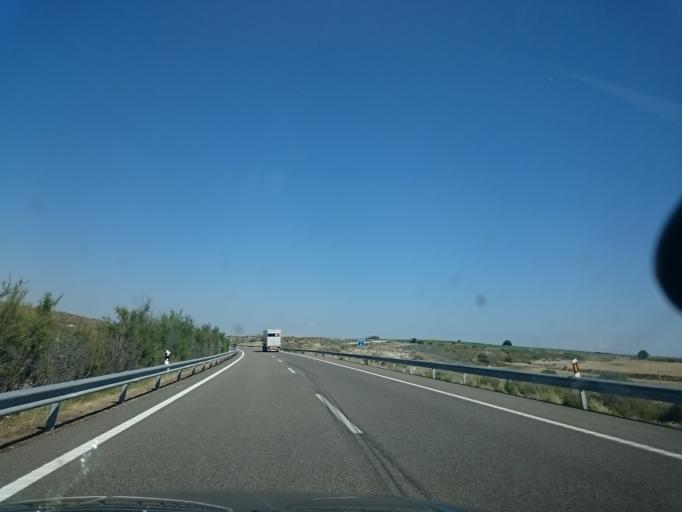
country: ES
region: Aragon
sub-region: Provincia de Huesca
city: Penalba
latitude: 41.5128
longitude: -0.0725
